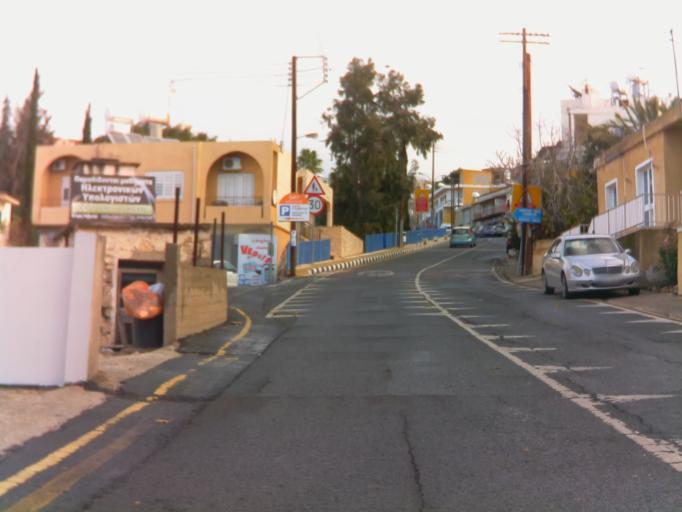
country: CY
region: Pafos
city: Pegeia
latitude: 34.8831
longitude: 32.3808
